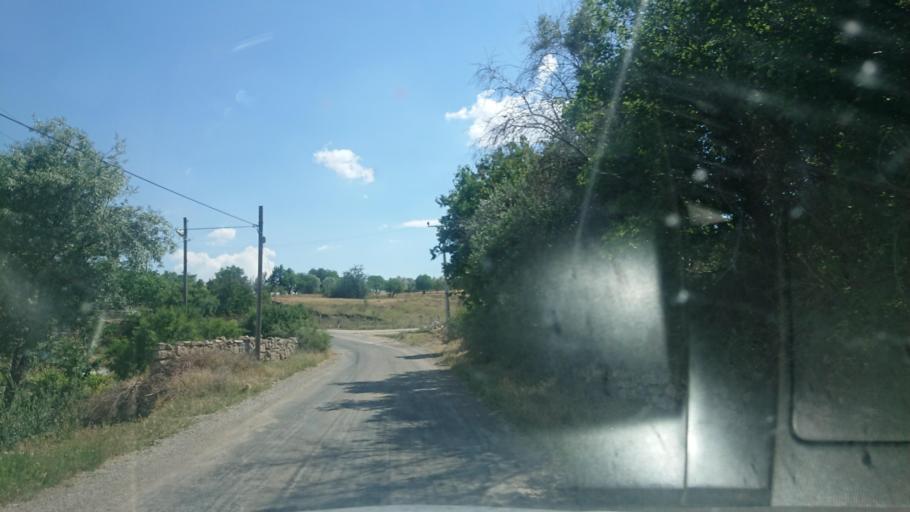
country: TR
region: Aksaray
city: Agacoren
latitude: 38.7670
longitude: 33.7844
